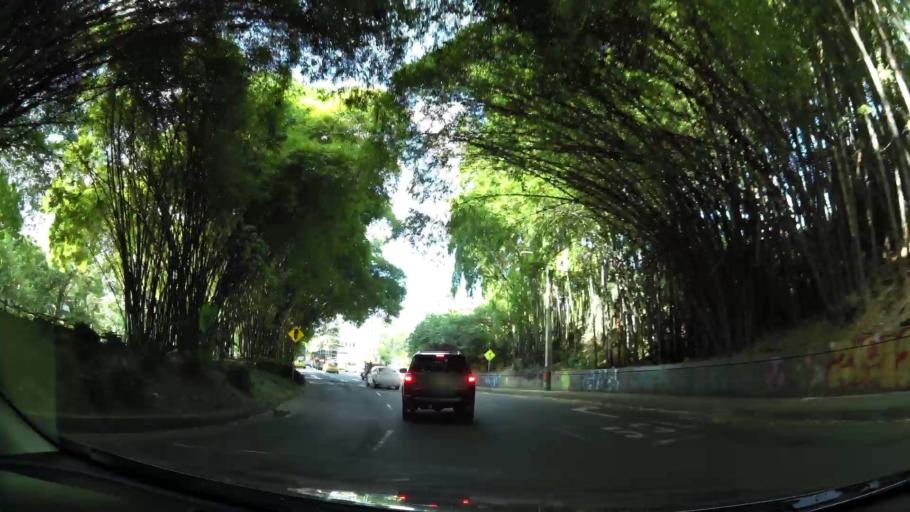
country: CO
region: Antioquia
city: Envigado
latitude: 6.1649
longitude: -75.5802
